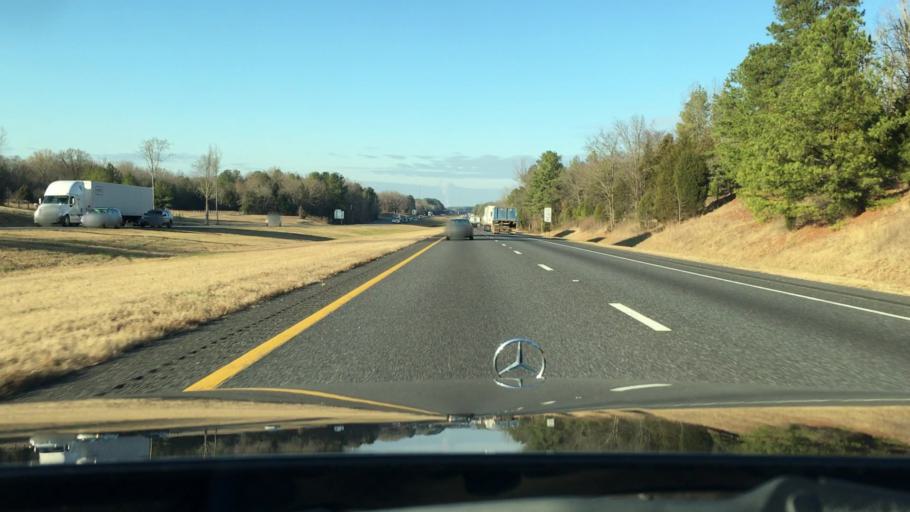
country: US
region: South Carolina
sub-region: York County
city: Lesslie
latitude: 34.7564
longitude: -81.0362
